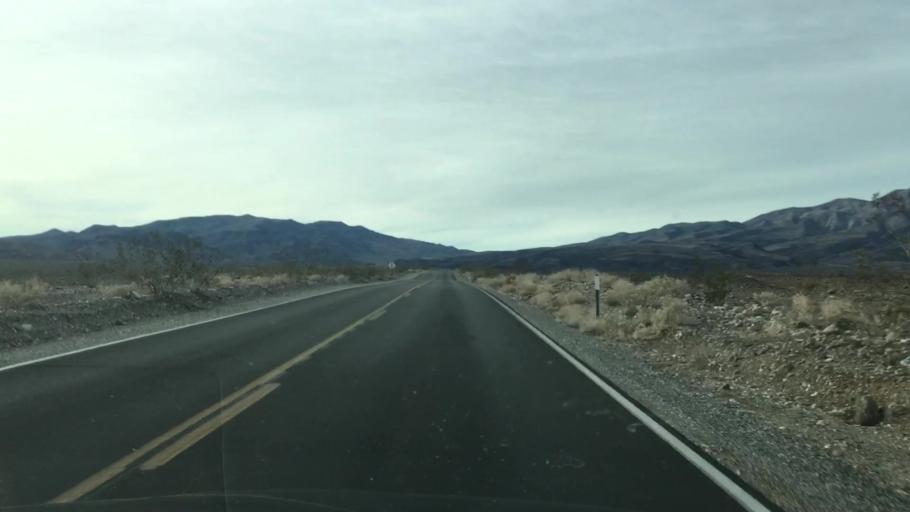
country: US
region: Nevada
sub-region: Nye County
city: Beatty
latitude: 36.5292
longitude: -117.2193
